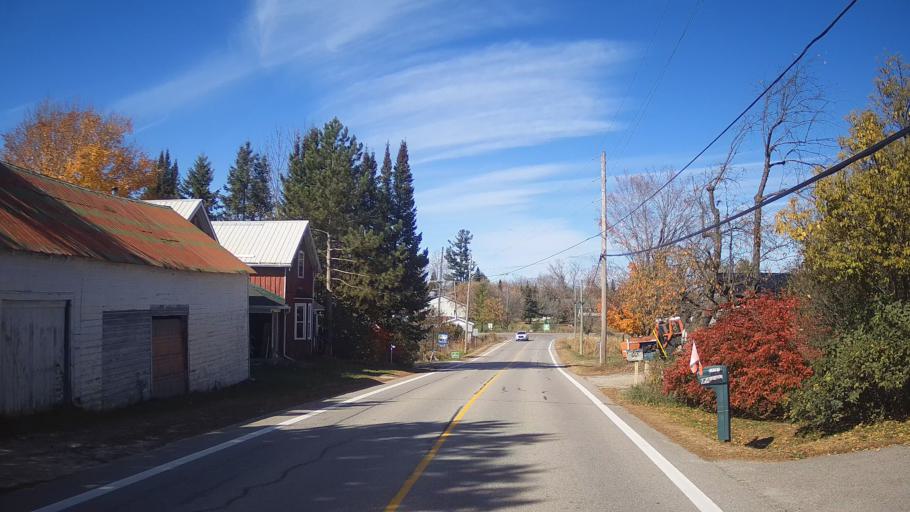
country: CA
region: Ontario
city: Perth
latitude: 44.8820
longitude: -76.3068
